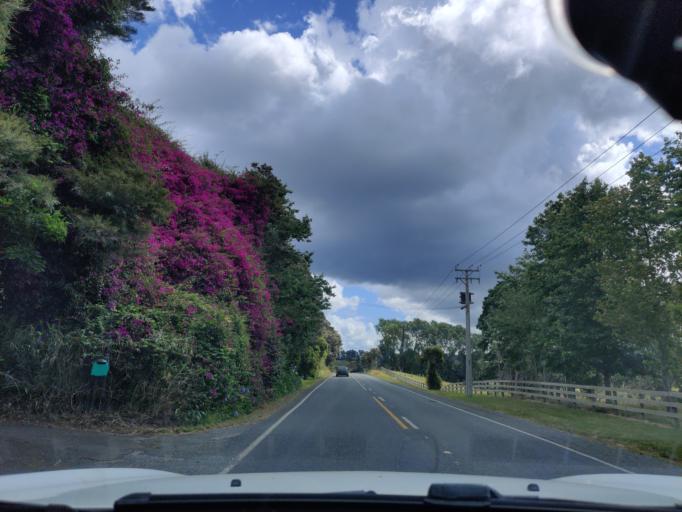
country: NZ
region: Auckland
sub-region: Auckland
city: Red Hill
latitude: -37.0375
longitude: 174.9945
